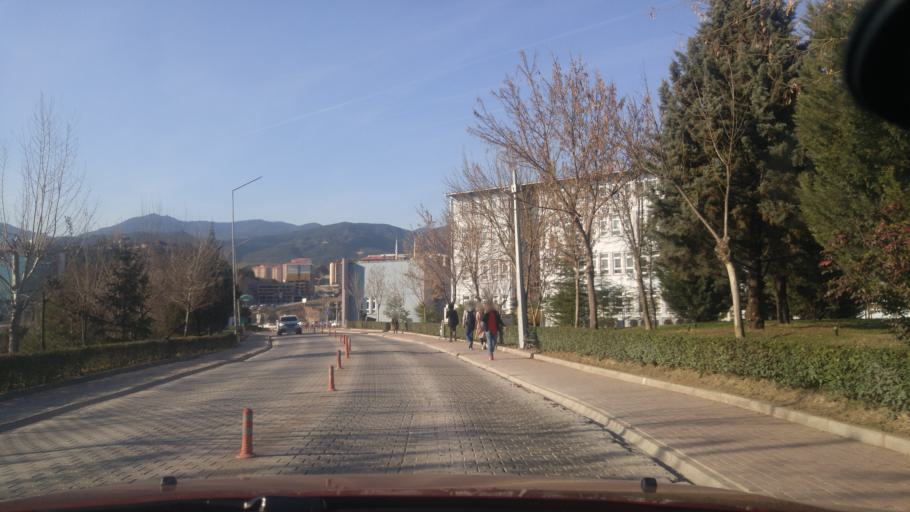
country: TR
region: Karabuk
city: Karabuk
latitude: 41.2136
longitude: 32.6522
